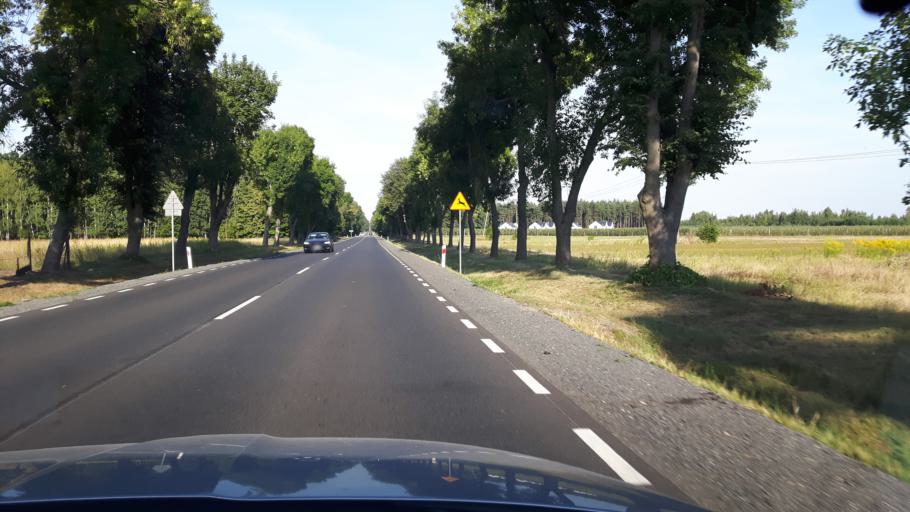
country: PL
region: Masovian Voivodeship
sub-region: Powiat legionowski
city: Wieliszew
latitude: 52.5013
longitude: 20.9407
